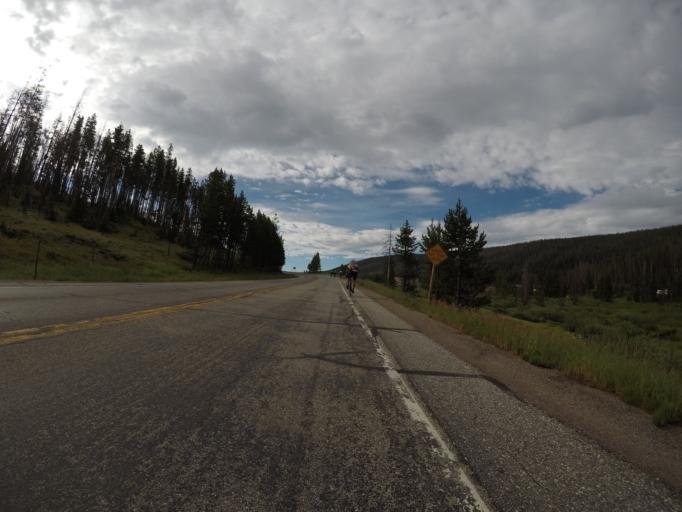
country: US
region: Wyoming
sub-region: Carbon County
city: Saratoga
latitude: 41.3256
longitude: -106.5064
